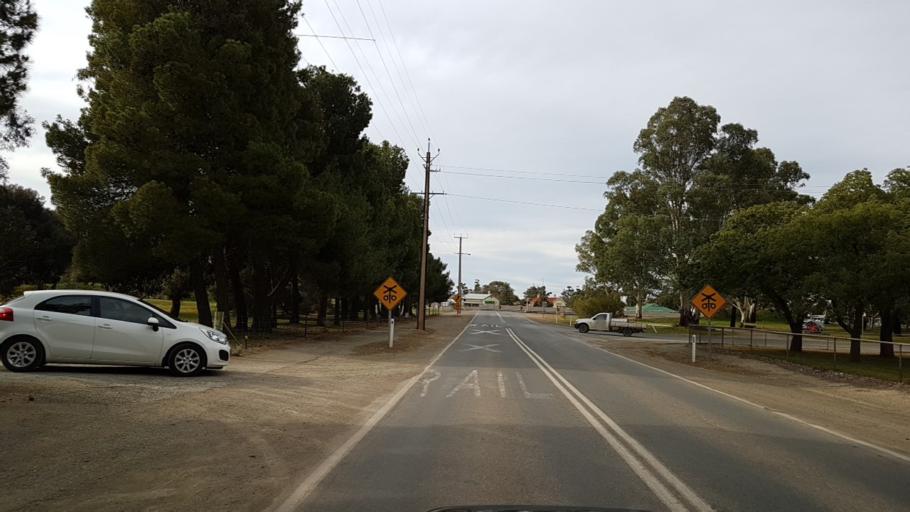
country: AU
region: South Australia
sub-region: Northern Areas
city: Jamestown
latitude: -33.2020
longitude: 138.6037
